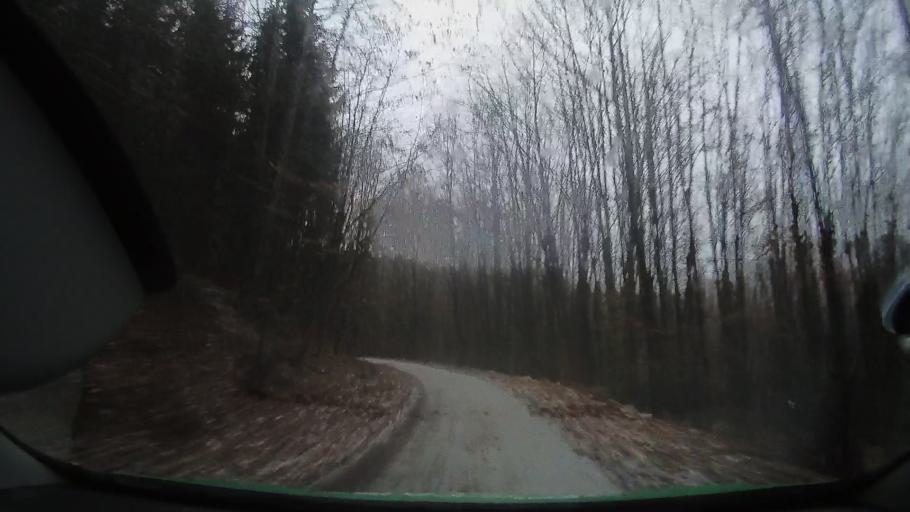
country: RO
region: Alba
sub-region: Comuna Avram Iancu
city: Avram Iancu
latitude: 46.3118
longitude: 22.7952
